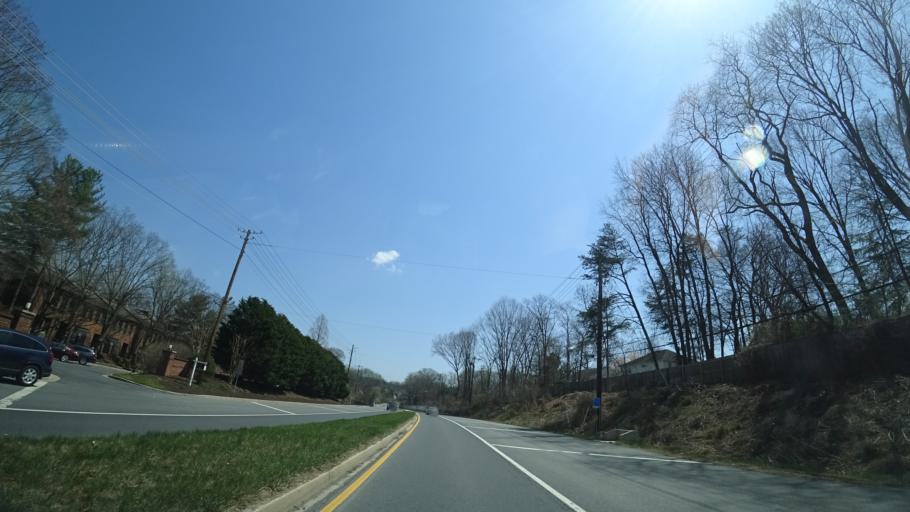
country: US
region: Maryland
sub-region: Montgomery County
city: Cabin John
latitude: 39.0103
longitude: -77.1539
